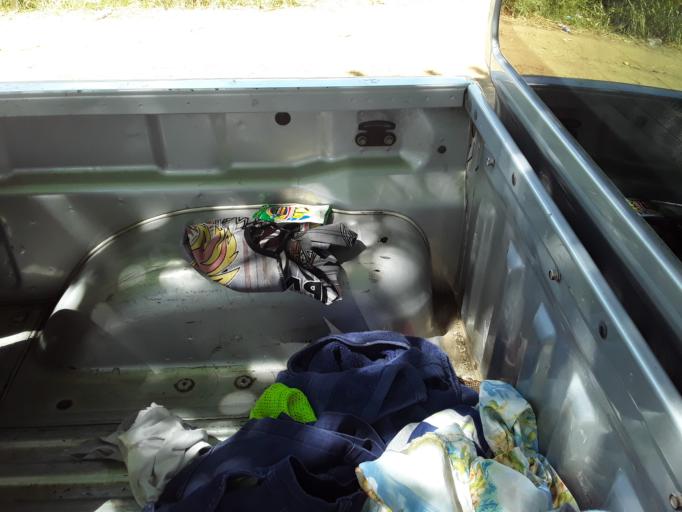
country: PG
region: National Capital
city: Port Moresby
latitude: -9.3905
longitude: 147.2704
